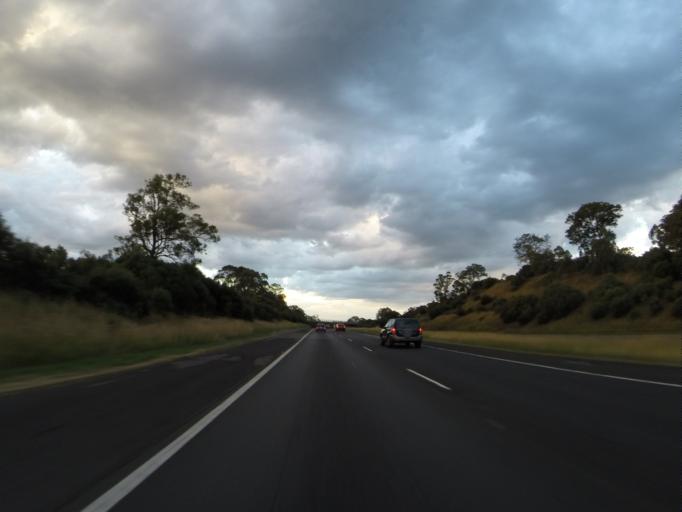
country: AU
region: New South Wales
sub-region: Campbelltown Municipality
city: Glen Alpine
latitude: -34.1098
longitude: 150.7609
